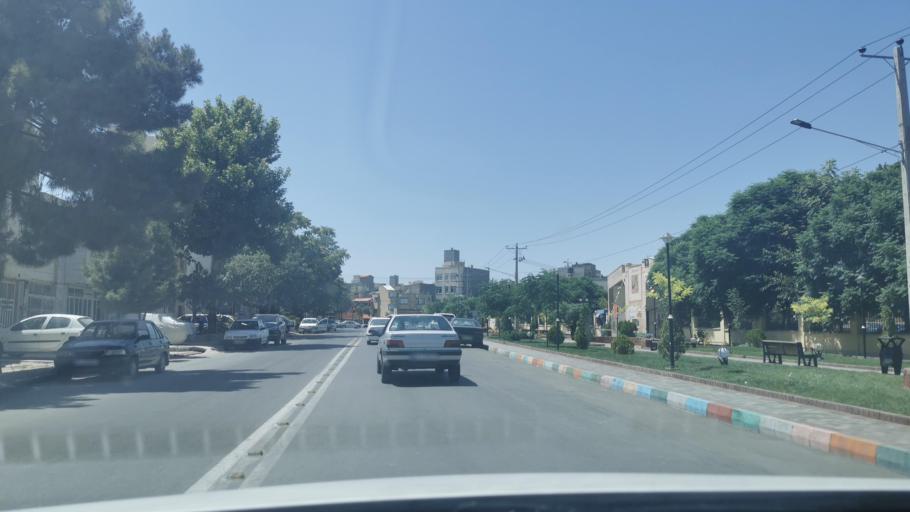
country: IR
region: Razavi Khorasan
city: Mashhad
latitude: 36.2755
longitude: 59.5779
